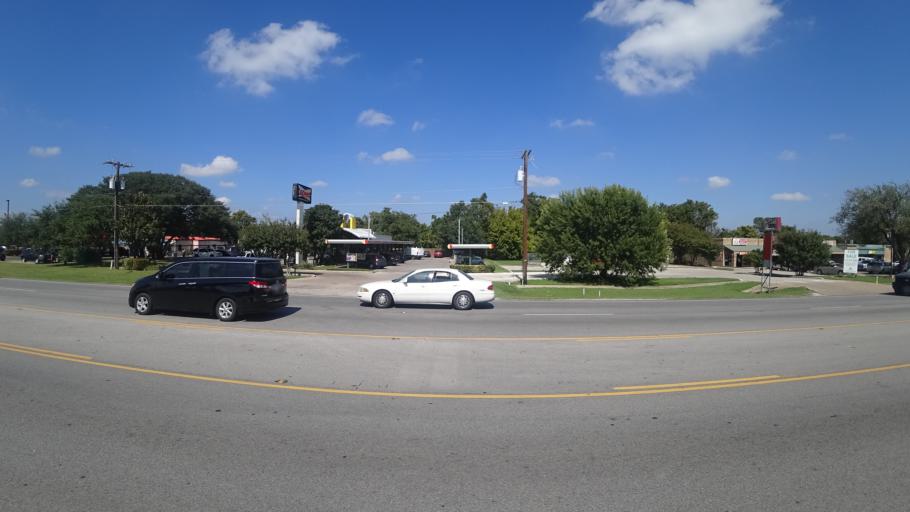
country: US
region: Texas
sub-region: Williamson County
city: Round Rock
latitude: 30.5118
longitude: -97.6967
